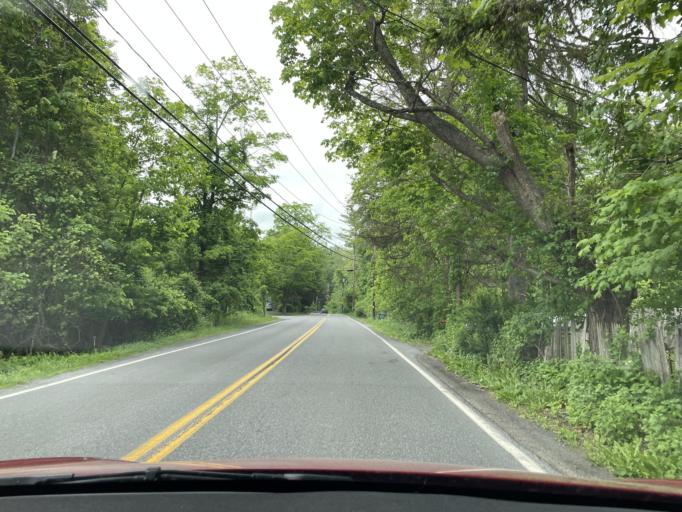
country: US
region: New York
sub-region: Ulster County
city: Zena
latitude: 42.0173
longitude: -74.0767
